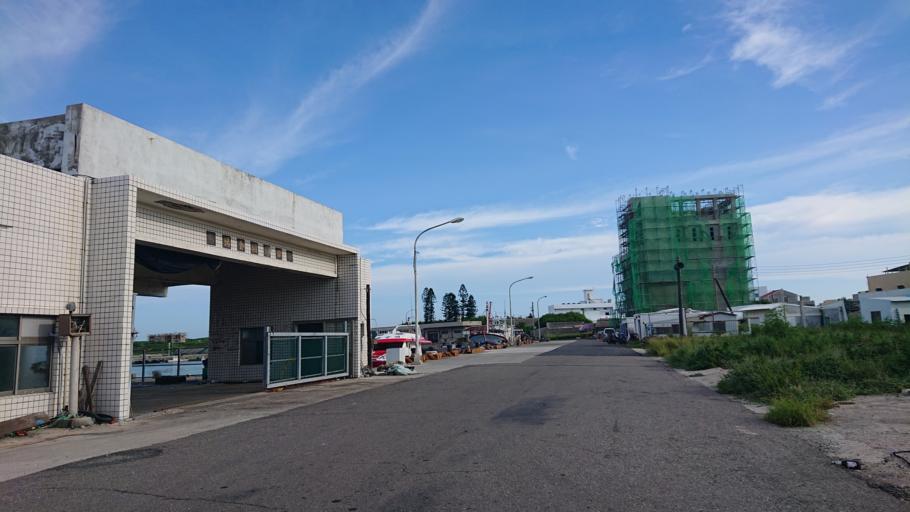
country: TW
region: Taiwan
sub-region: Penghu
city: Ma-kung
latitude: 23.5261
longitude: 119.6046
